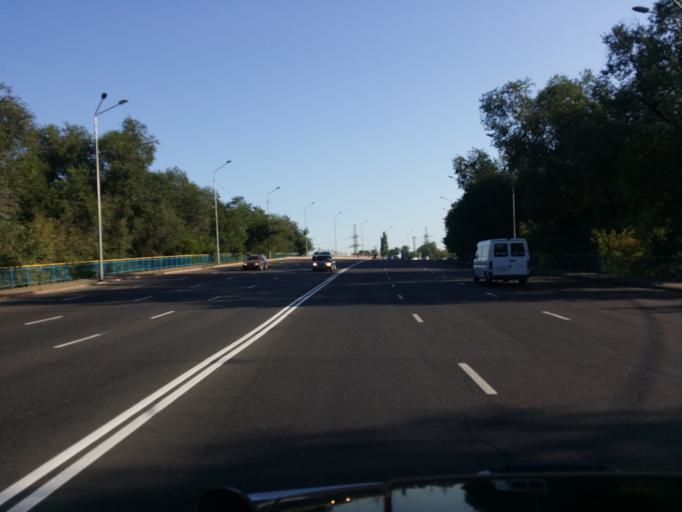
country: KZ
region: Almaty Oblysy
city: Pervomayskiy
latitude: 43.3444
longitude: 76.9325
